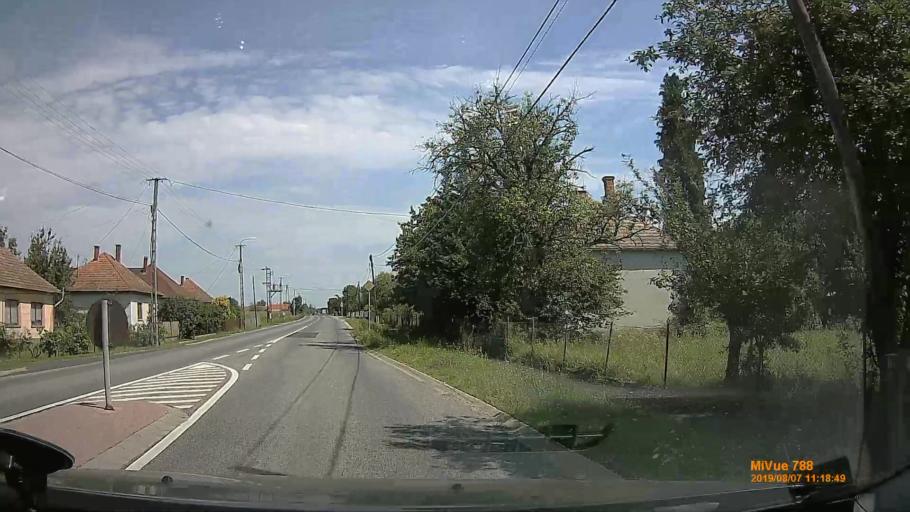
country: HU
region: Zala
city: Zalalovo
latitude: 46.7572
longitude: 16.5617
